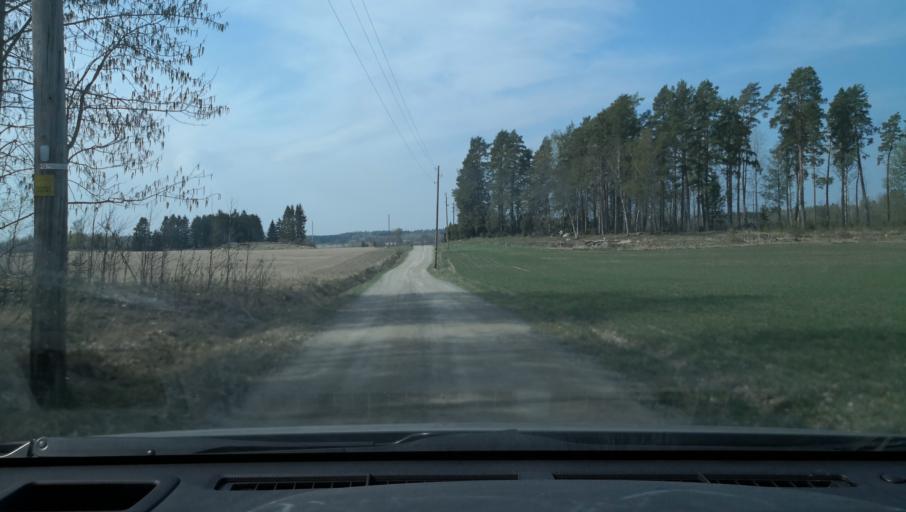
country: SE
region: Vaestmanland
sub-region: Vasteras
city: Skultuna
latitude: 59.7766
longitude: 16.4092
